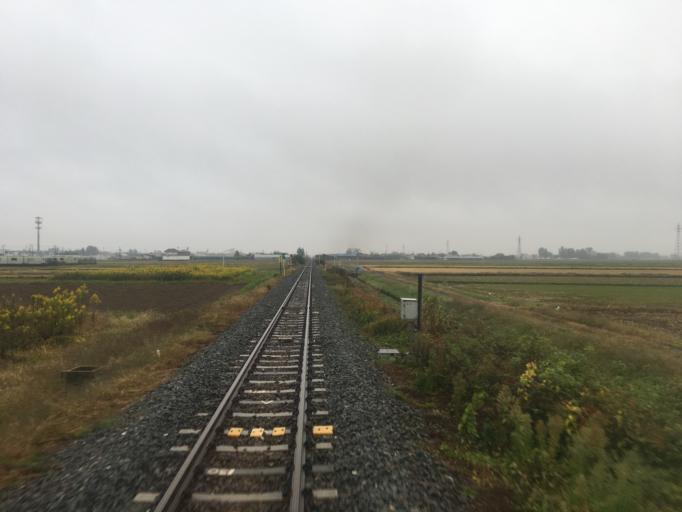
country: JP
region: Miyagi
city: Furukawa
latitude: 38.5665
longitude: 140.9937
